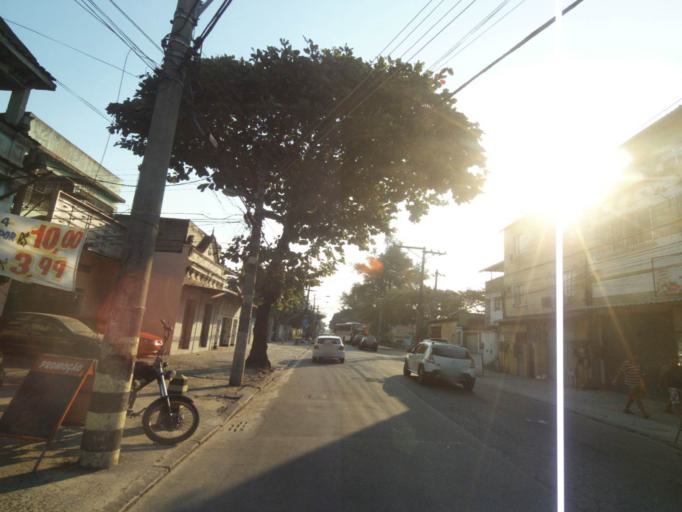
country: BR
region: Rio de Janeiro
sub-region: Nilopolis
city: Nilopolis
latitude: -22.8766
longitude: -43.4262
